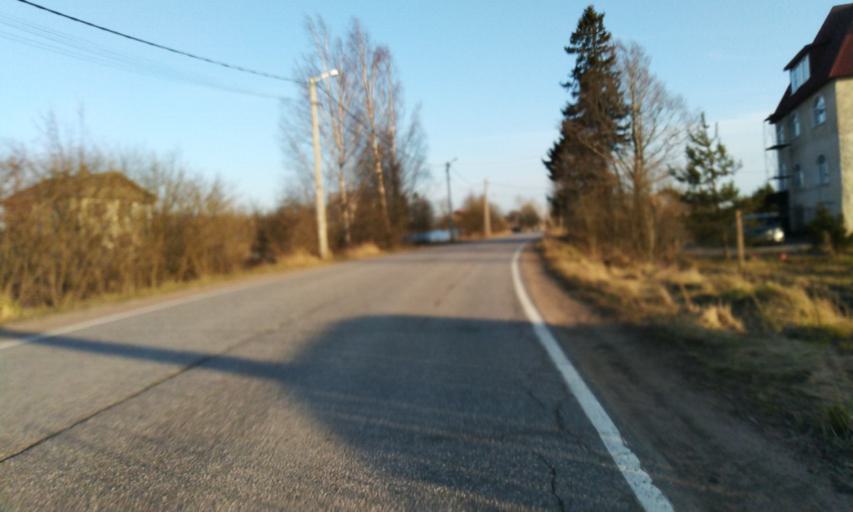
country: RU
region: Leningrad
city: Novoye Devyatkino
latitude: 60.1013
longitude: 30.4477
